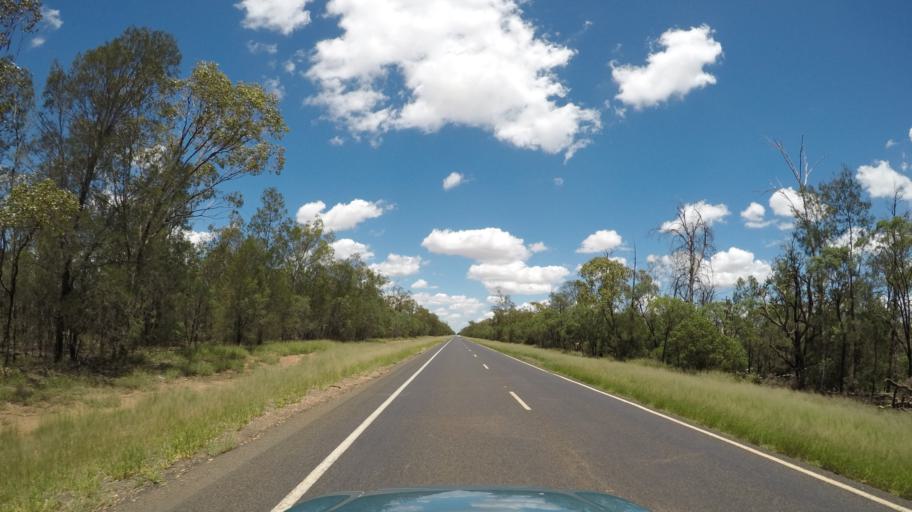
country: AU
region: Queensland
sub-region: Goondiwindi
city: Goondiwindi
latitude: -28.1601
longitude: 150.6317
